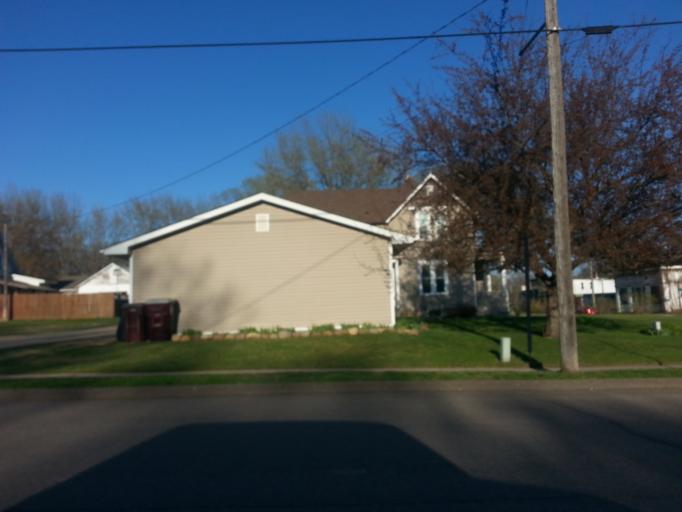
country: US
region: Minnesota
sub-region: Goodhue County
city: Cannon Falls
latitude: 44.5262
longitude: -93.0198
